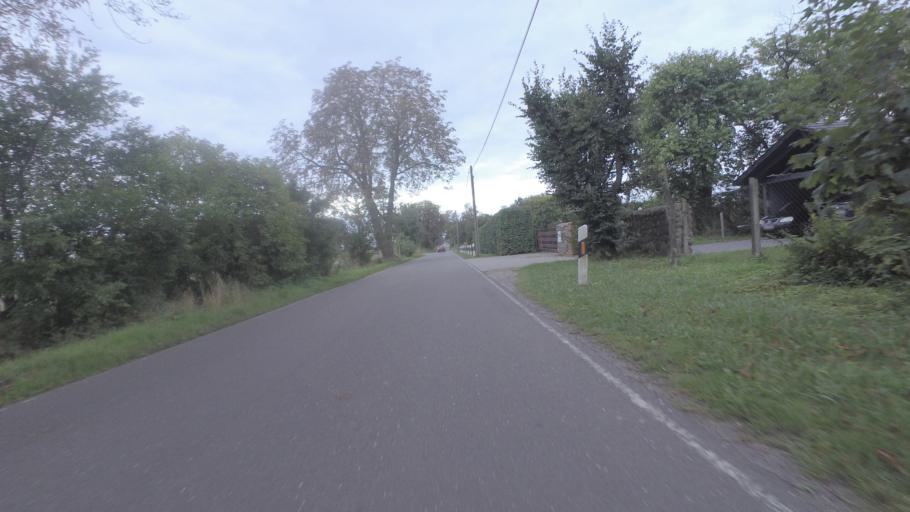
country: DE
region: Brandenburg
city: Neuenhagen
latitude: 52.5707
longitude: 13.6638
